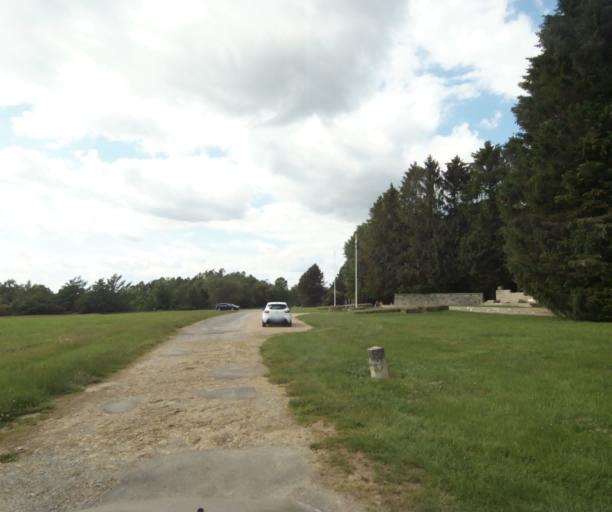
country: FR
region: Champagne-Ardenne
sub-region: Departement des Ardennes
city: Montcy-Notre-Dame
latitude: 49.7643
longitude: 4.7371
